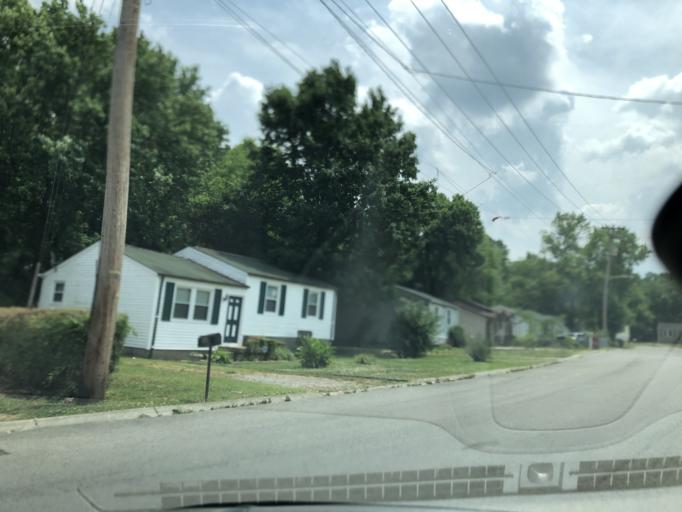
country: US
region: Tennessee
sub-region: Davidson County
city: Oak Hill
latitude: 36.0628
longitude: -86.6924
